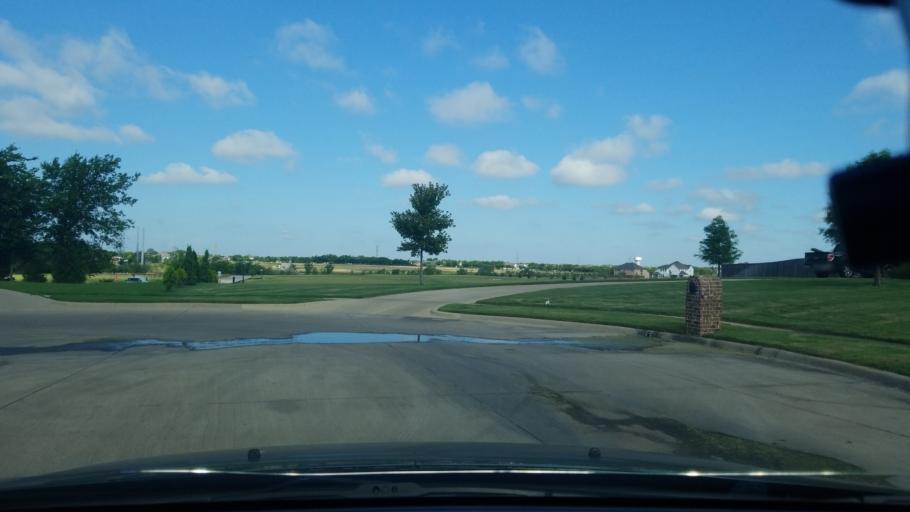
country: US
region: Texas
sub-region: Dallas County
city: Sunnyvale
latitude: 32.8042
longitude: -96.5689
